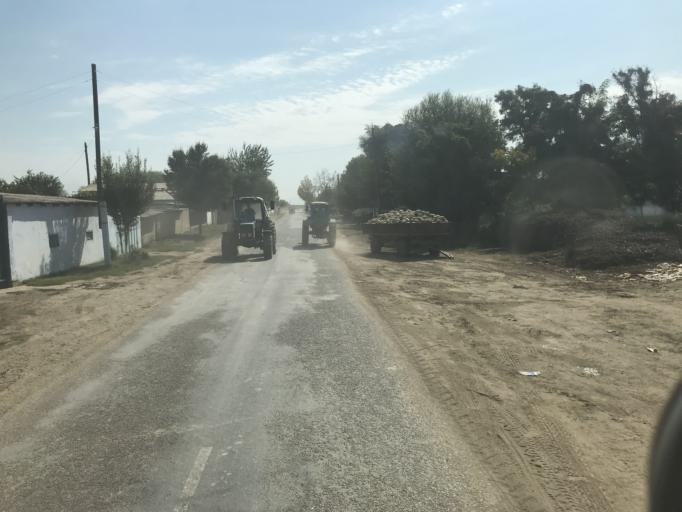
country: KZ
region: Ongtustik Qazaqstan
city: Myrzakent
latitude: 40.6642
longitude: 68.6265
